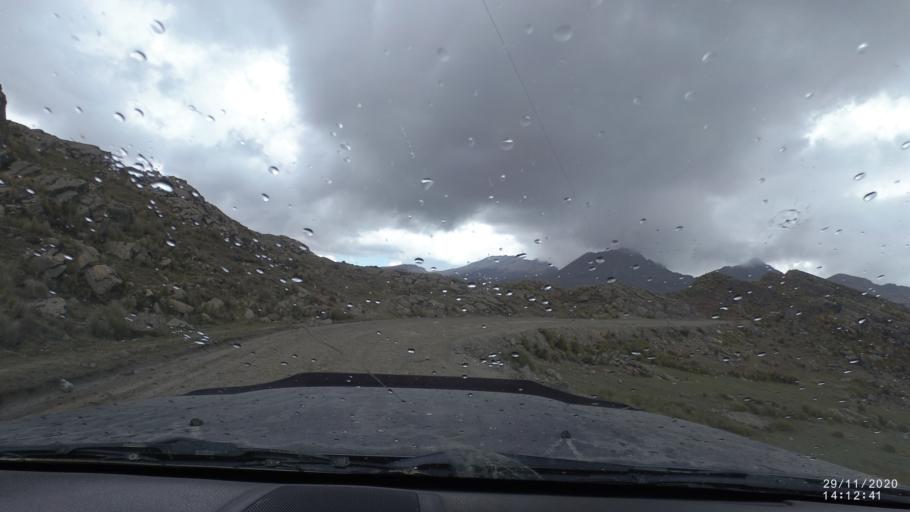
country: BO
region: Cochabamba
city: Sipe Sipe
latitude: -17.2399
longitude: -66.3945
